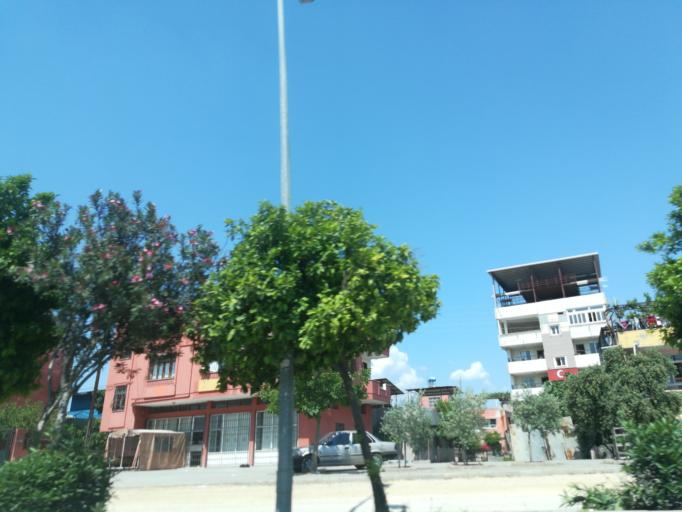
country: TR
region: Adana
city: Yuregir
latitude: 37.0146
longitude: 35.3857
